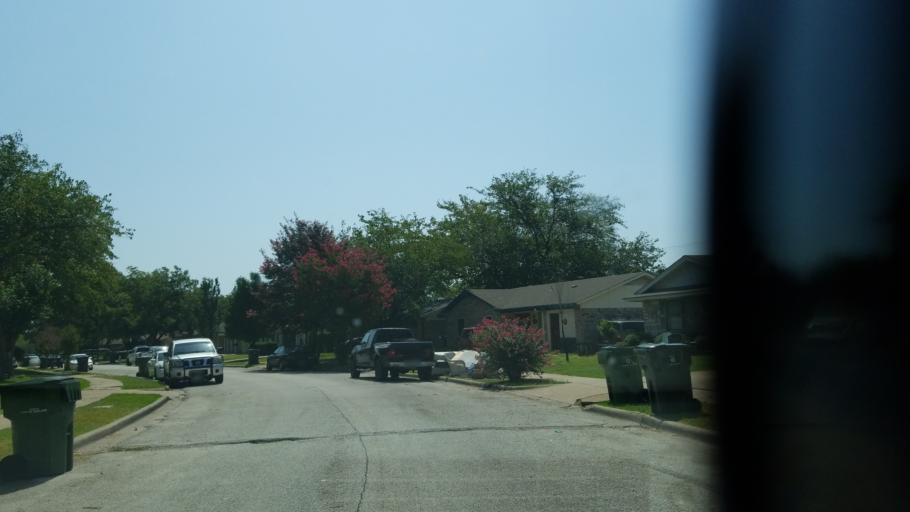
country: US
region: Texas
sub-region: Dallas County
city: Garland
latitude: 32.9159
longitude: -96.6244
